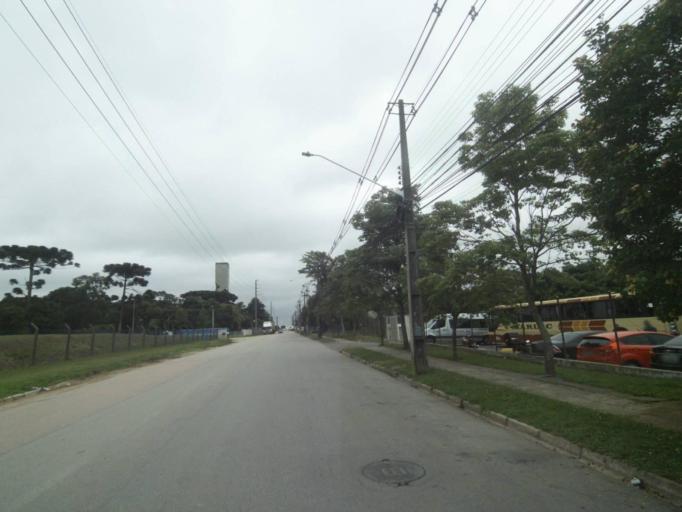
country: BR
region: Parana
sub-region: Sao Jose Dos Pinhais
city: Sao Jose dos Pinhais
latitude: -25.5578
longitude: -49.3098
